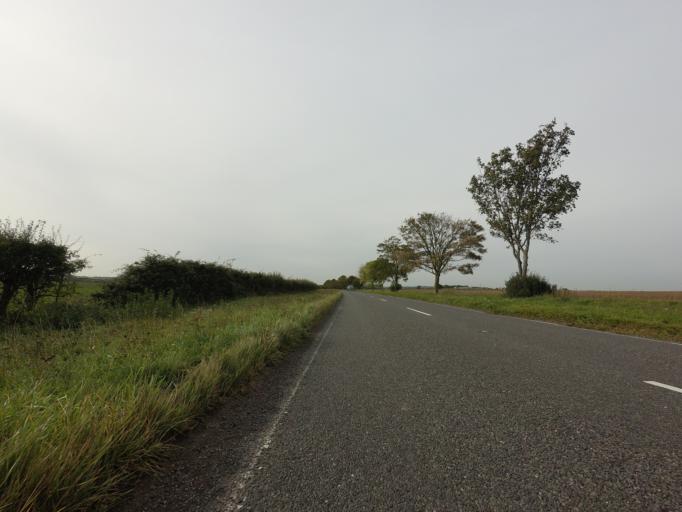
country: GB
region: England
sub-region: Cambridgeshire
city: Melbourn
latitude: 52.0739
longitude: 0.0627
